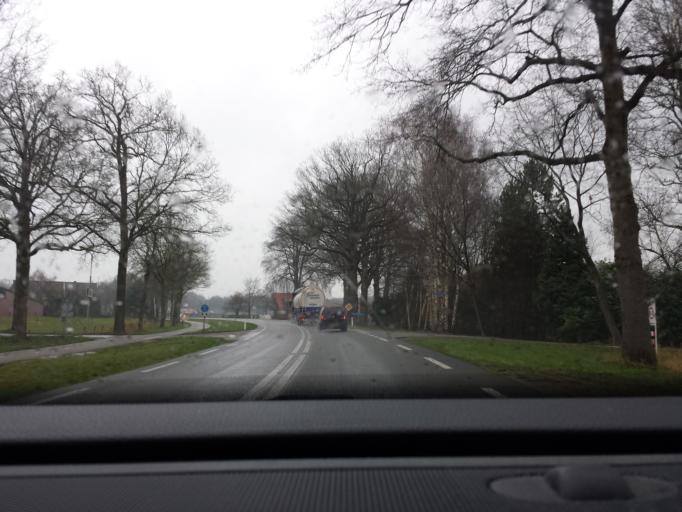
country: NL
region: Gelderland
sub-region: Gemeente Bronckhorst
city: Hengelo
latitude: 52.0866
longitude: 6.3165
